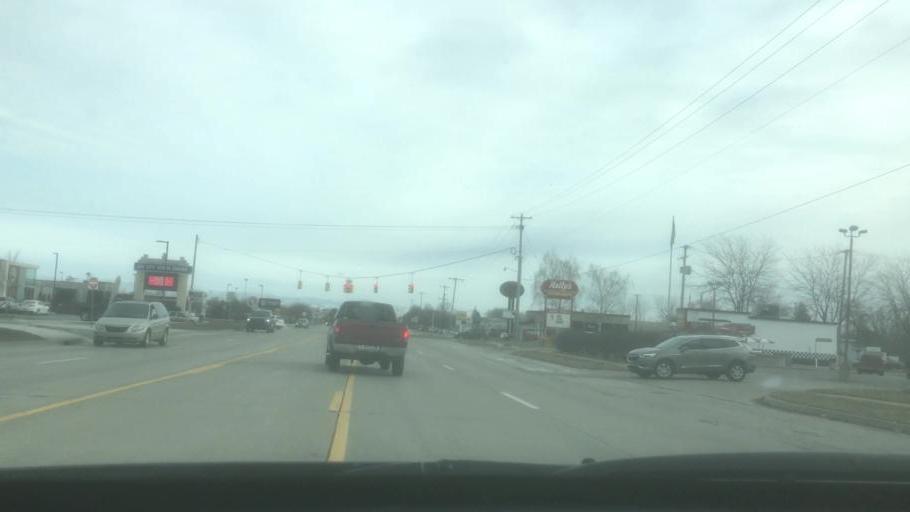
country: US
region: Michigan
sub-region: Bay County
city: Bay City
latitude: 43.6238
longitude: -83.8957
